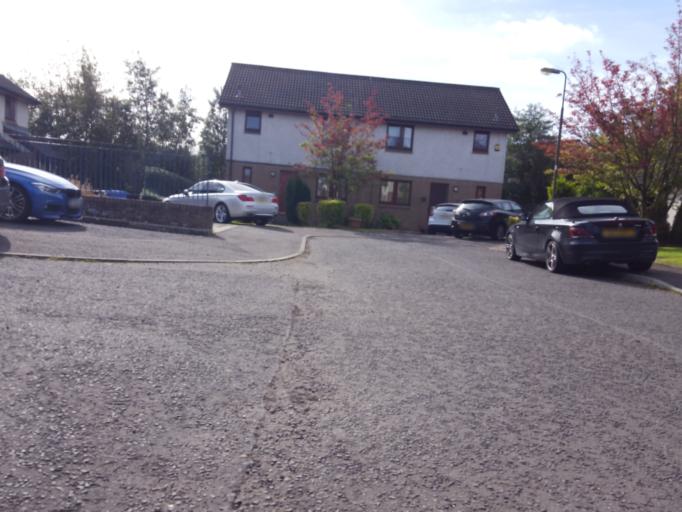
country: GB
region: Scotland
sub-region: West Lothian
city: Livingston
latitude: 55.8904
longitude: -3.5423
